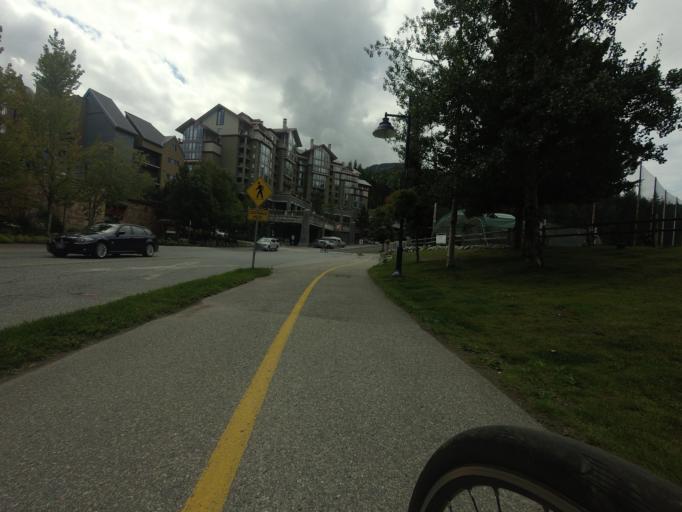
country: CA
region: British Columbia
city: Whistler
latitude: 50.1130
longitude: -122.9569
